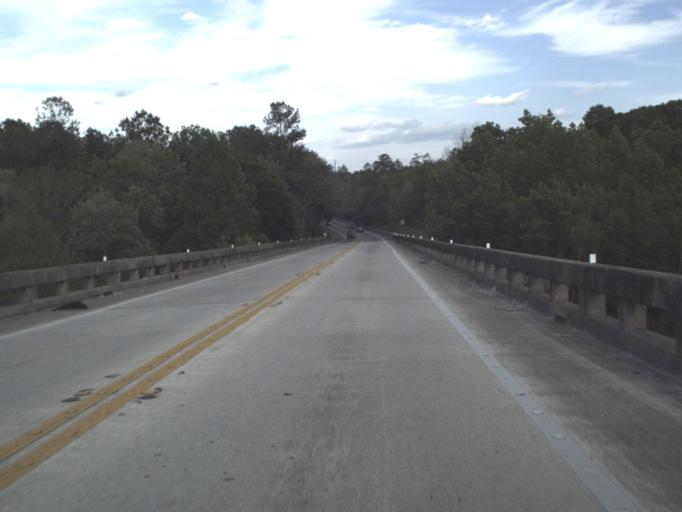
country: US
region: Florida
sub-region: Marion County
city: Silver Springs Shores
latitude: 29.2150
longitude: -81.9868
